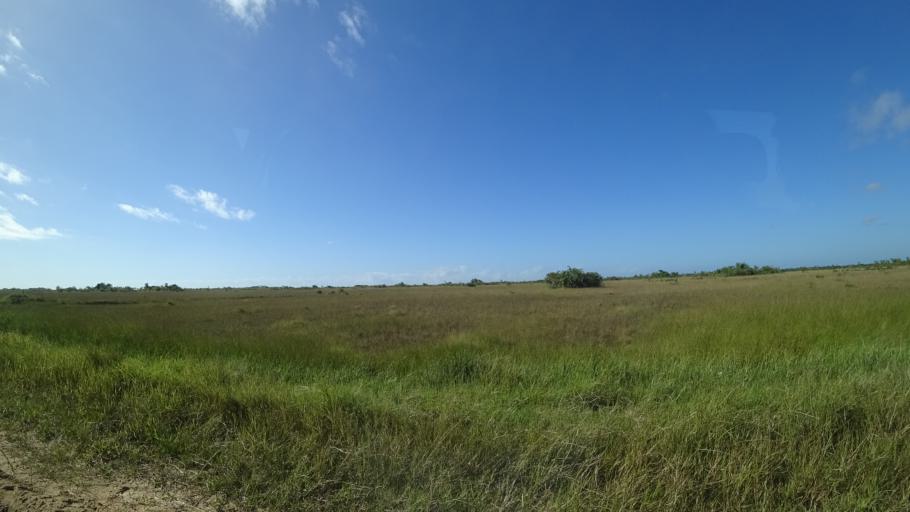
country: MZ
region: Sofala
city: Beira
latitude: -19.6985
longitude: 35.0297
